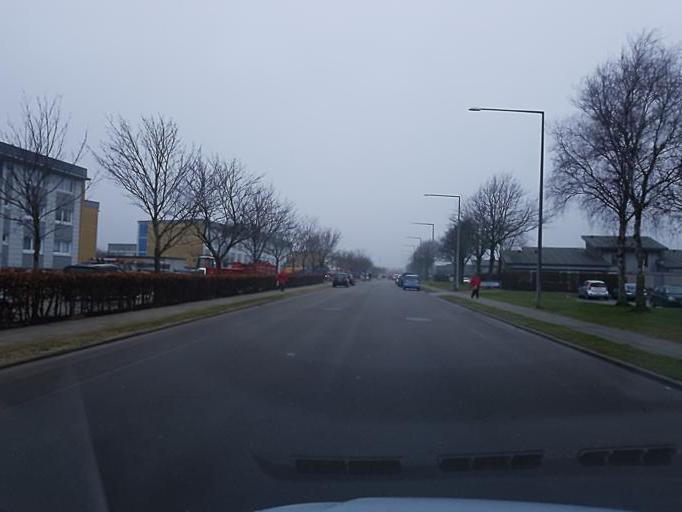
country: DK
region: South Denmark
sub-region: Esbjerg Kommune
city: Esbjerg
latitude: 55.4811
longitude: 8.4927
